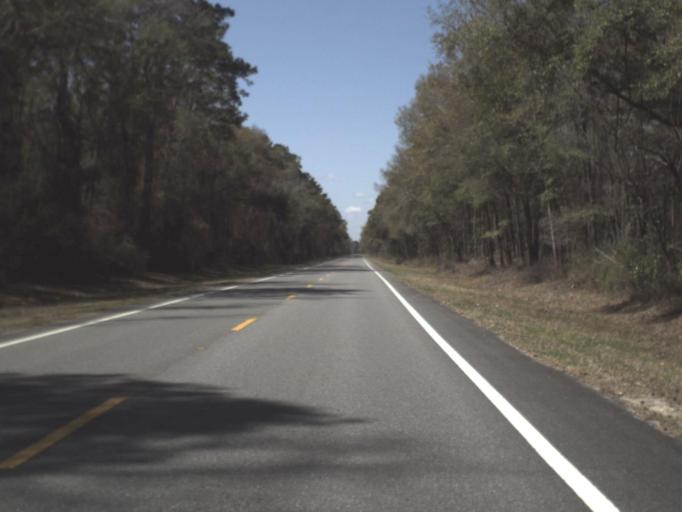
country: US
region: Florida
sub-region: Leon County
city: Woodville
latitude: 30.2431
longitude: -84.2910
